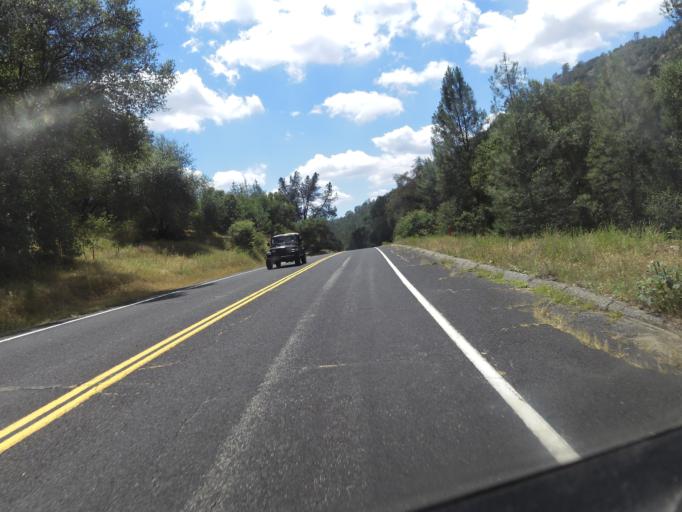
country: US
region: California
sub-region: Madera County
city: Coarsegold
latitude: 37.1823
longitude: -119.6258
